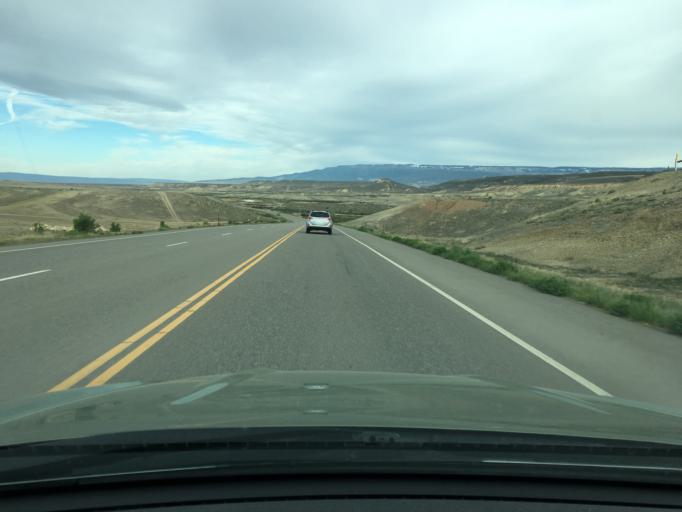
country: US
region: Colorado
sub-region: Delta County
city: Orchard City
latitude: 38.8008
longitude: -107.8630
